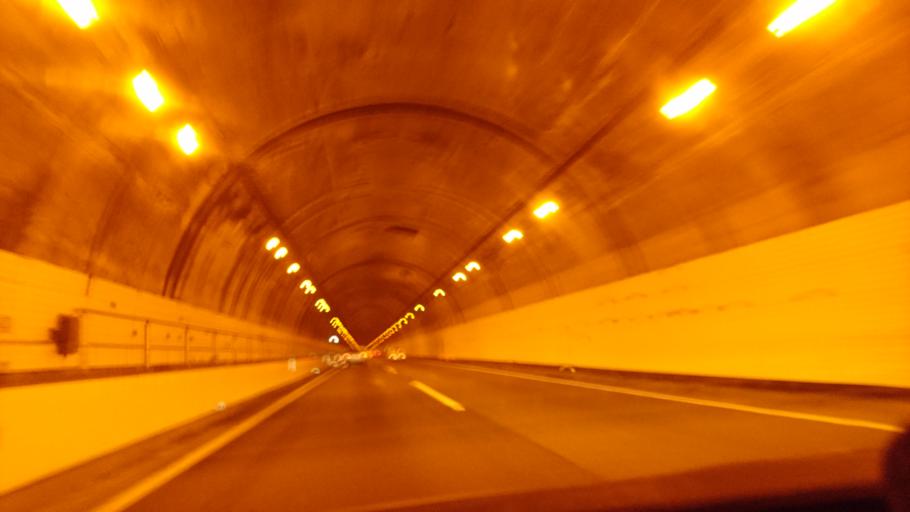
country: JP
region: Iwate
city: Ichinoseki
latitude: 38.9498
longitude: 141.1054
